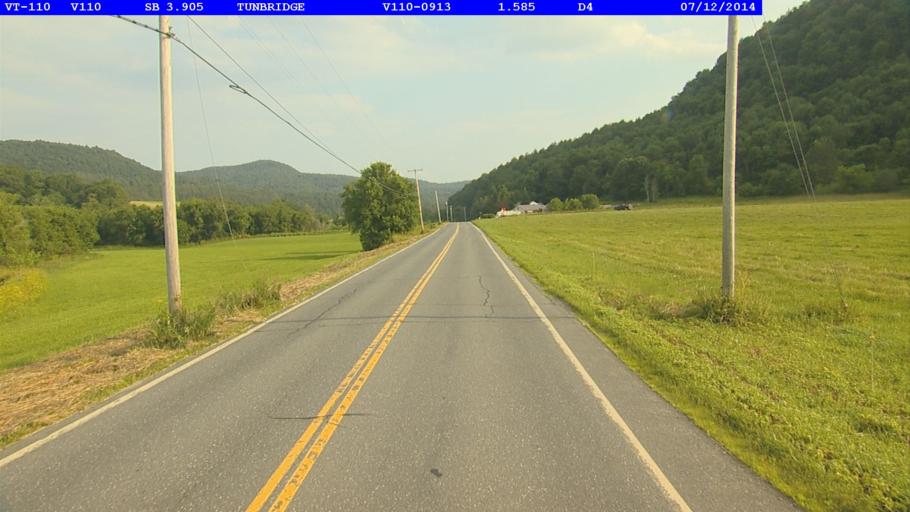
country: US
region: Vermont
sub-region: Orange County
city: Chelsea
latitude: 43.8736
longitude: -72.4988
